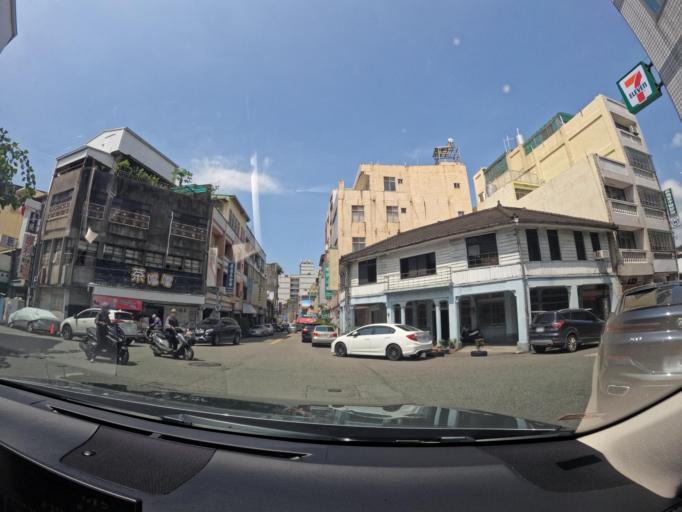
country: TW
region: Taiwan
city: Fengyuan
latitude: 24.3110
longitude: 120.8276
